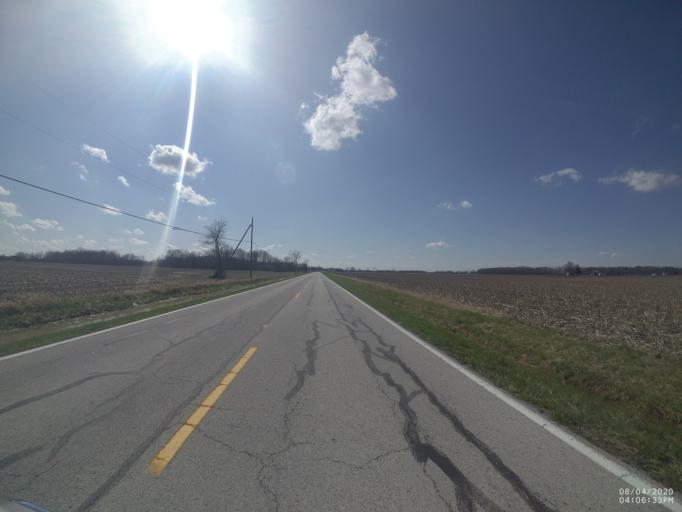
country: US
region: Ohio
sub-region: Sandusky County
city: Ballville
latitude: 41.2683
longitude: -83.2110
